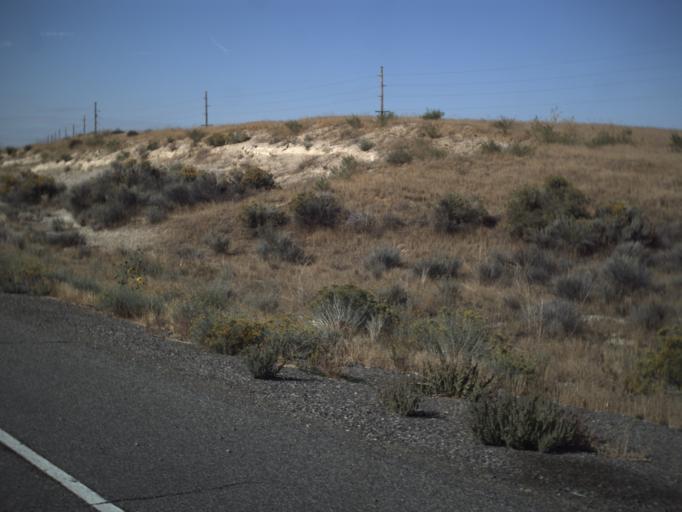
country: US
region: Utah
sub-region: Tooele County
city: Grantsville
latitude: 40.7679
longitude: -112.9874
